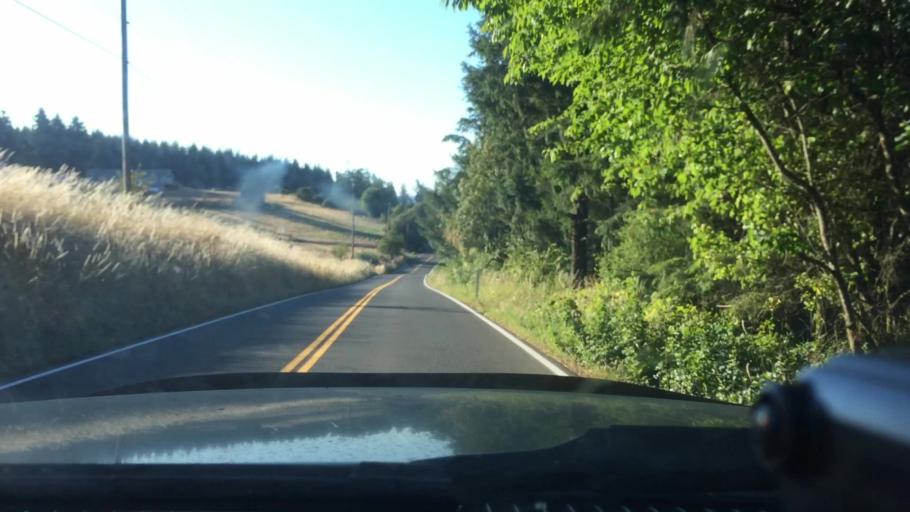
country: US
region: Oregon
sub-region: Yamhill County
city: Newberg
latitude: 45.3419
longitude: -122.9535
